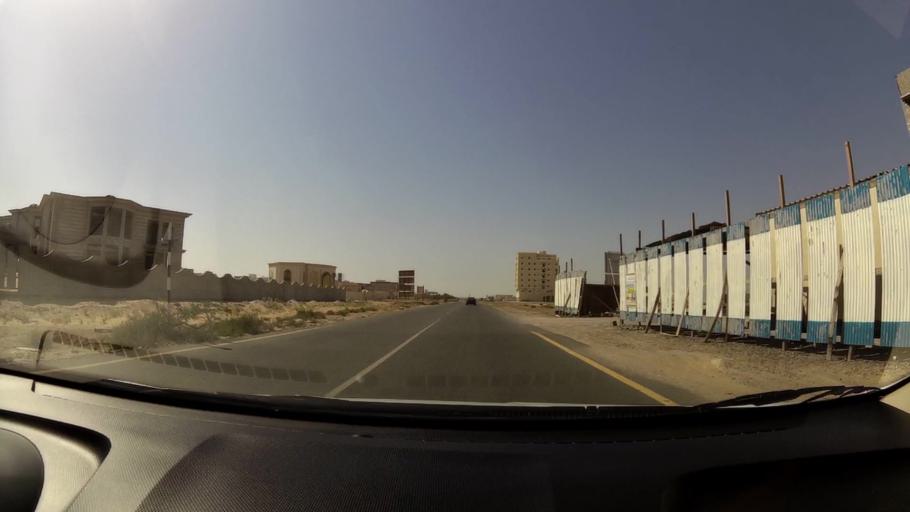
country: AE
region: Umm al Qaywayn
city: Umm al Qaywayn
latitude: 25.4930
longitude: 55.5993
